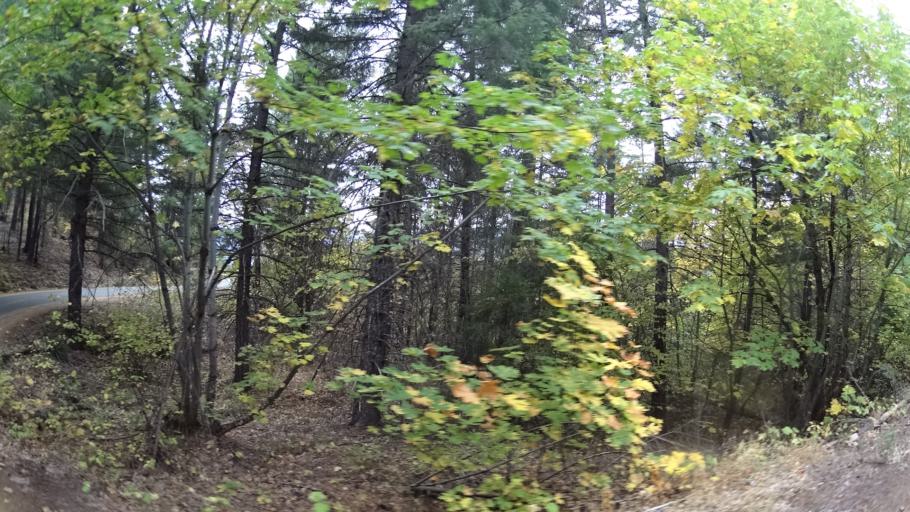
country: US
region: California
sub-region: Siskiyou County
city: Happy Camp
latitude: 41.8273
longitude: -123.3285
